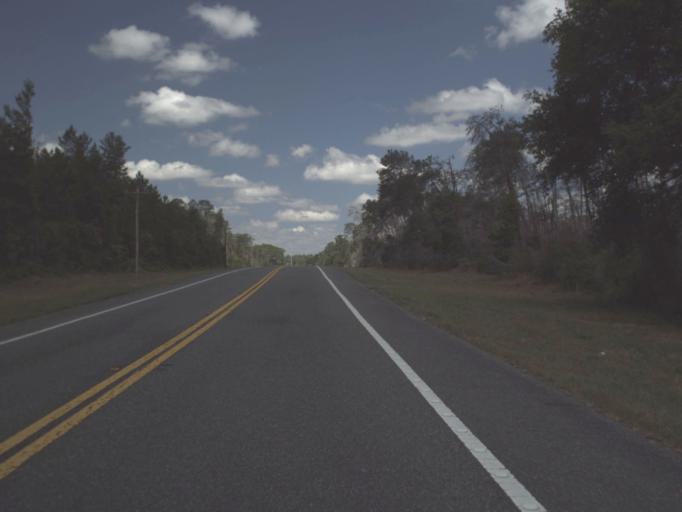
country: US
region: Florida
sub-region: Lake County
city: Astor
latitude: 29.1730
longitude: -81.6647
